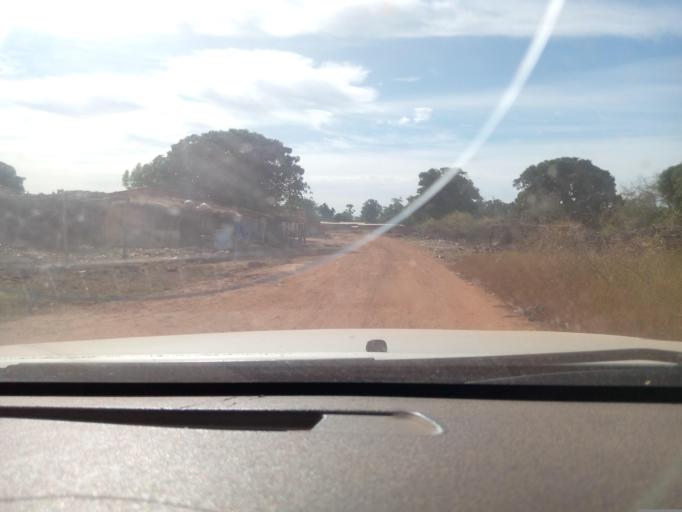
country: ML
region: Sikasso
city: Sikasso
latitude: 11.8963
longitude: -6.0516
